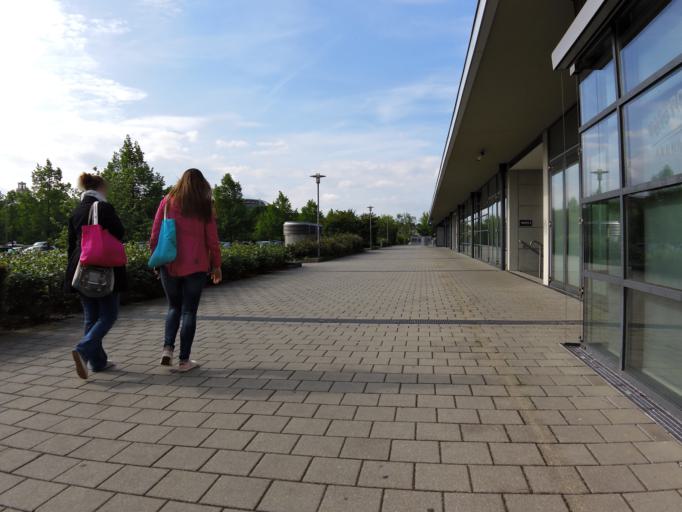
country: DE
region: Saxony
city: Leipzig
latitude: 51.3425
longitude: 12.3542
